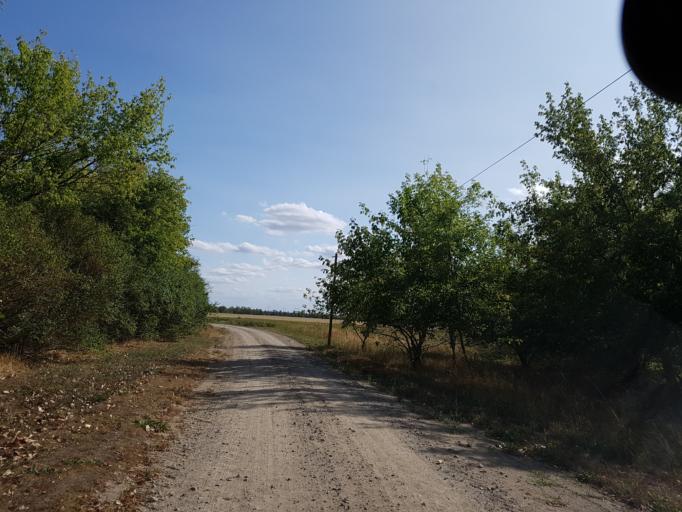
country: DE
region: Brandenburg
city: Treuenbrietzen
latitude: 51.9953
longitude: 12.8564
